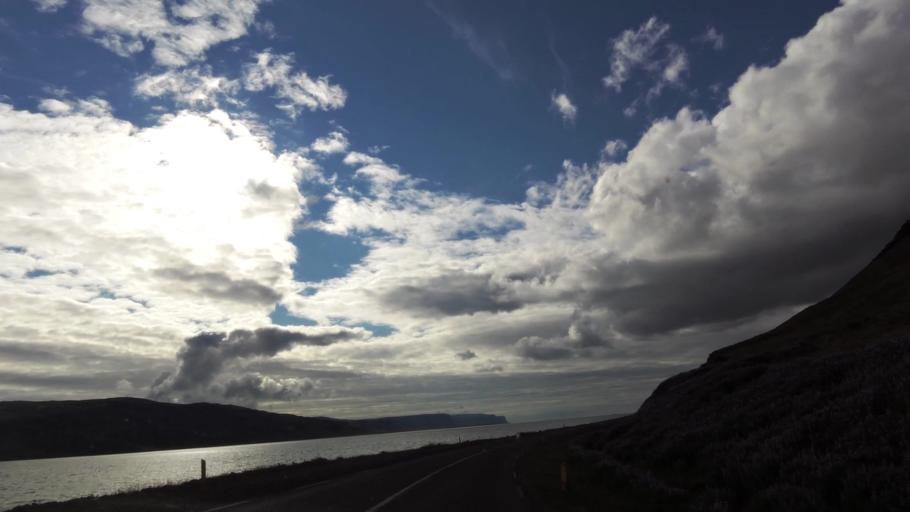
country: IS
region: West
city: Olafsvik
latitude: 65.5438
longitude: -23.8819
